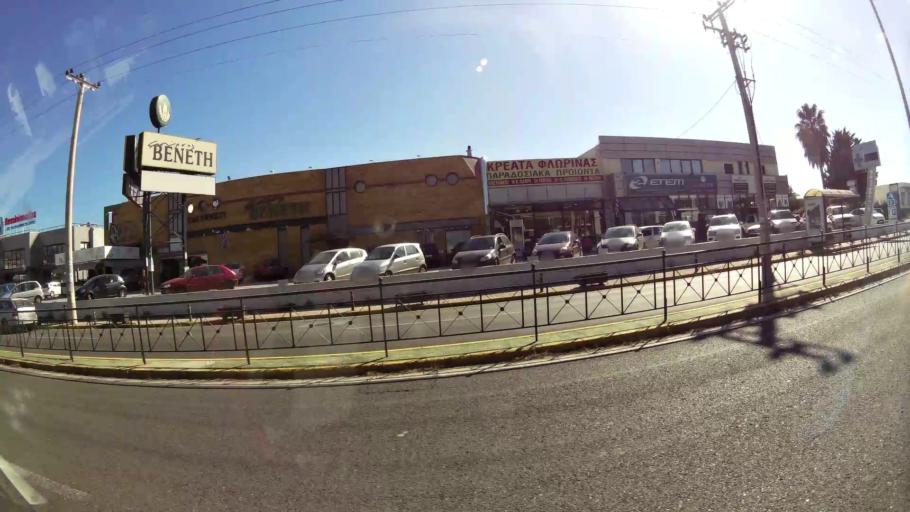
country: GR
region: Attica
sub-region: Nomarchia Anatolikis Attikis
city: Pikermi
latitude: 38.0013
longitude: 23.9384
